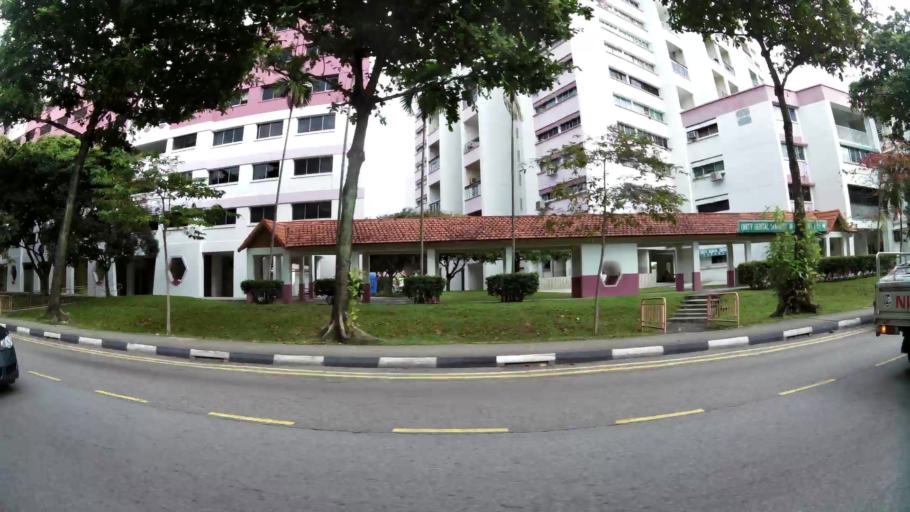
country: SG
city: Singapore
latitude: 1.3182
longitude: 103.8997
